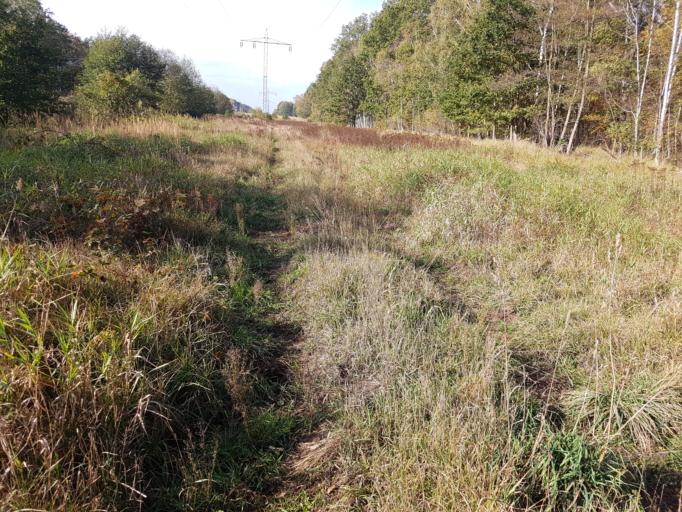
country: DE
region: Brandenburg
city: Schilda
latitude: 51.5889
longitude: 13.3392
